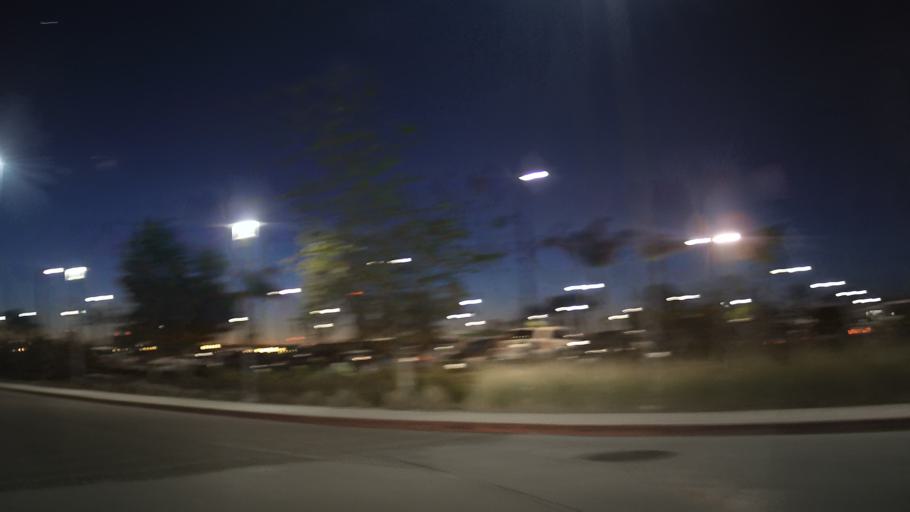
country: US
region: California
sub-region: San Diego County
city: San Diego
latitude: 32.7376
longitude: -117.1829
